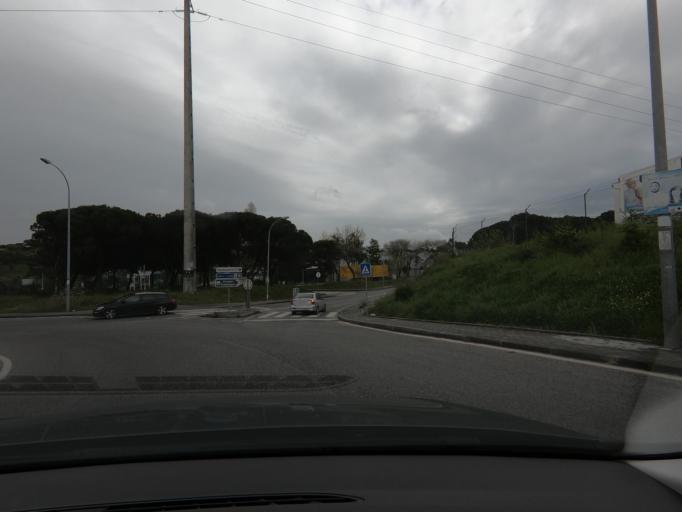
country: PT
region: Lisbon
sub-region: Sintra
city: Rio de Mouro
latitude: 38.7543
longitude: -9.3440
